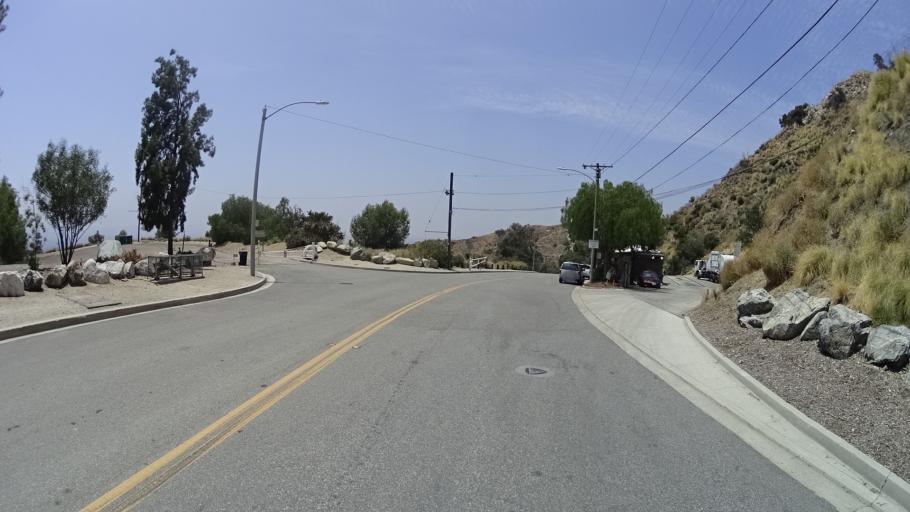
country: US
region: California
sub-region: Los Angeles County
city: Burbank
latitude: 34.2056
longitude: -118.3107
